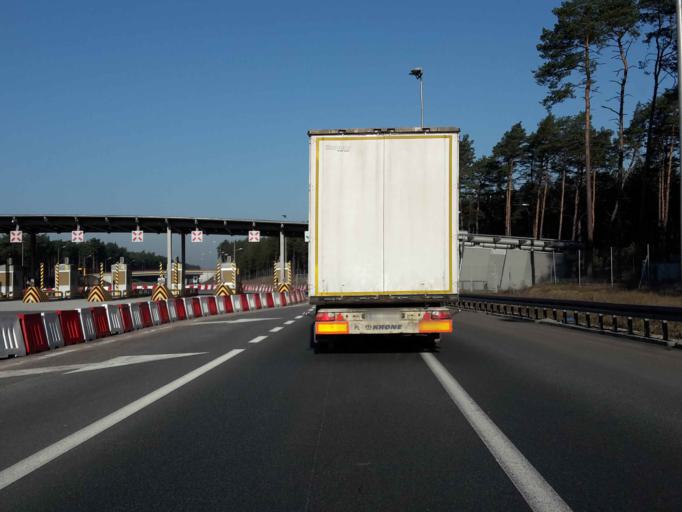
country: PL
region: Kujawsko-Pomorskie
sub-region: Torun
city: Torun
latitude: 52.9676
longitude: 18.6713
